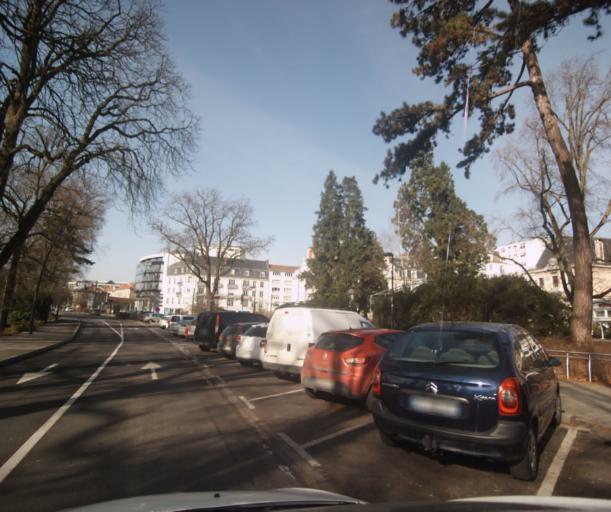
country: FR
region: Franche-Comte
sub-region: Departement du Doubs
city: Besancon
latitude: 47.2422
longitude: 6.0311
